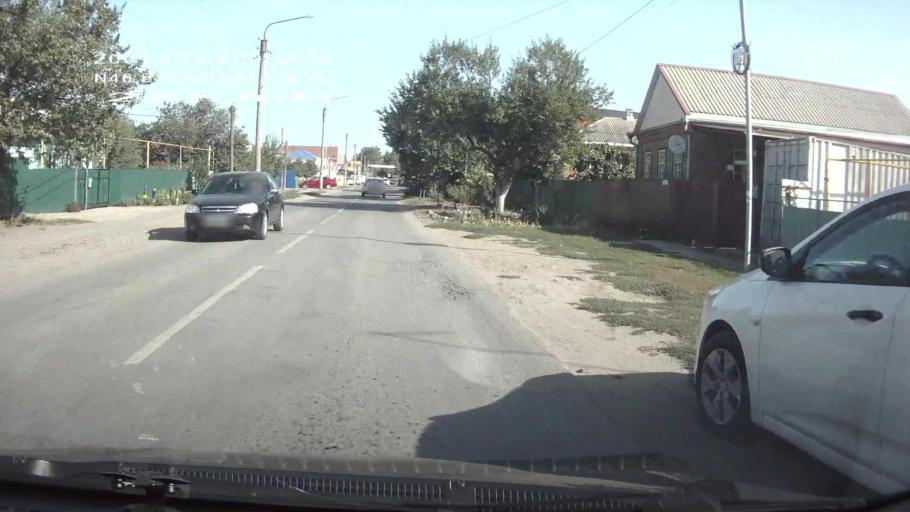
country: RU
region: Rostov
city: Tselina
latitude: 46.5348
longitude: 41.0267
